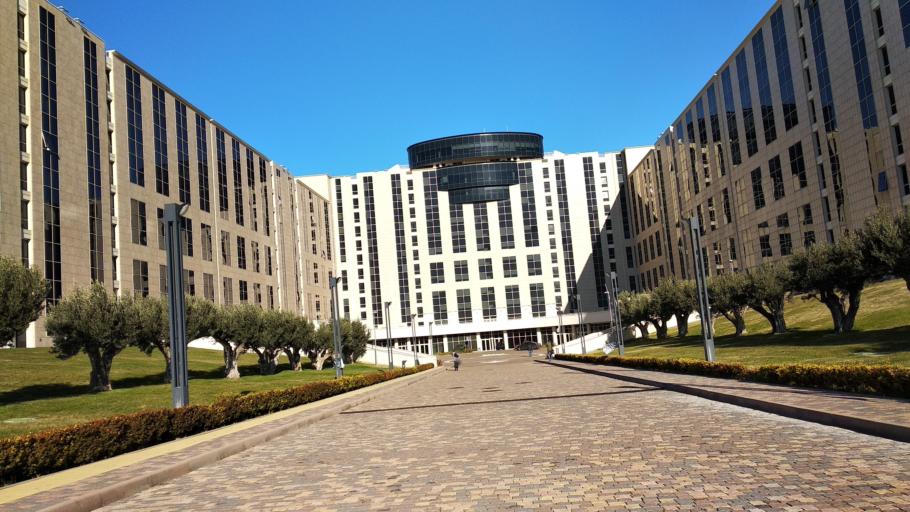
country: IT
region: Calabria
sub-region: Provincia di Catanzaro
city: Catanzaro
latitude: 38.8595
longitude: 16.5727
